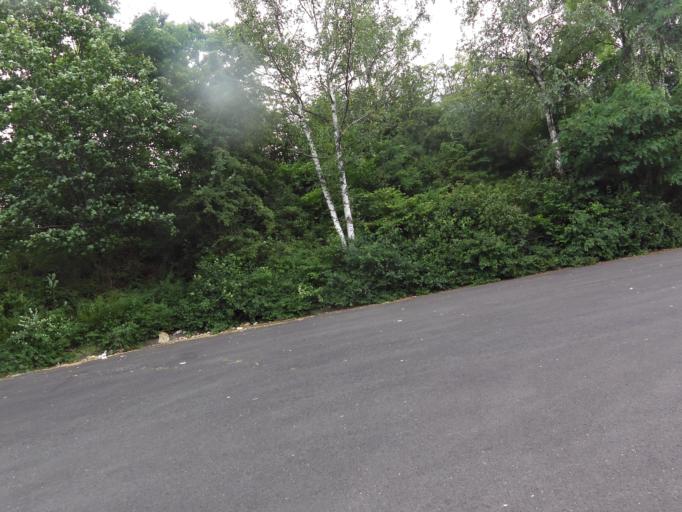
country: DE
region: Bavaria
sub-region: Regierungsbezirk Unterfranken
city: Wuerzburg
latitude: 49.7673
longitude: 9.9355
